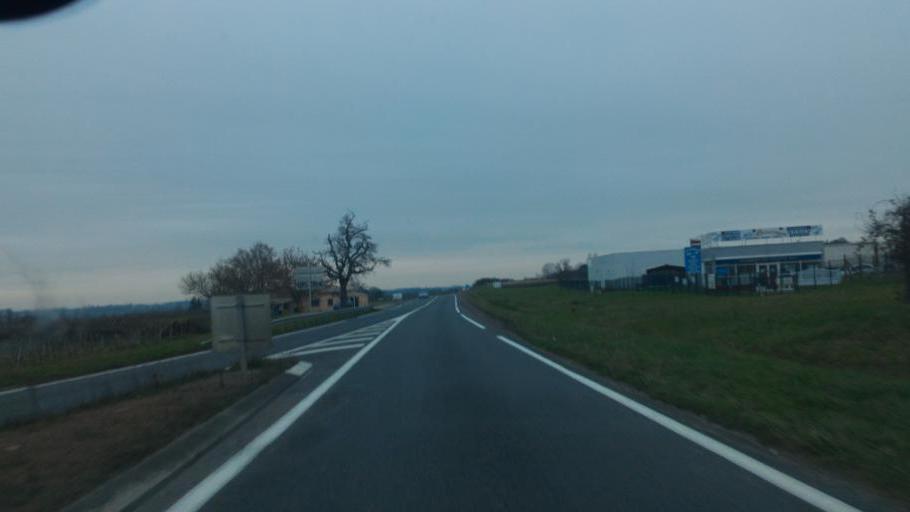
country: FR
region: Aquitaine
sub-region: Departement de la Gironde
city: Berson
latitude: 45.1201
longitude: -0.5718
